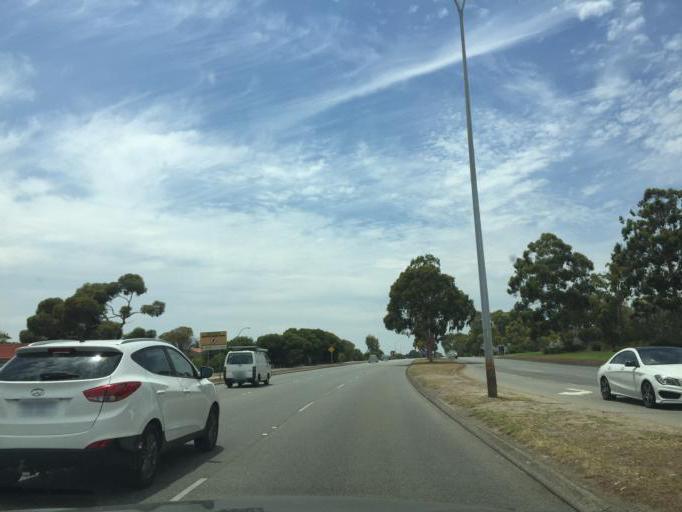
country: AU
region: Western Australia
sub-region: Melville
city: Winthrop
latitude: -32.0639
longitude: 115.8362
